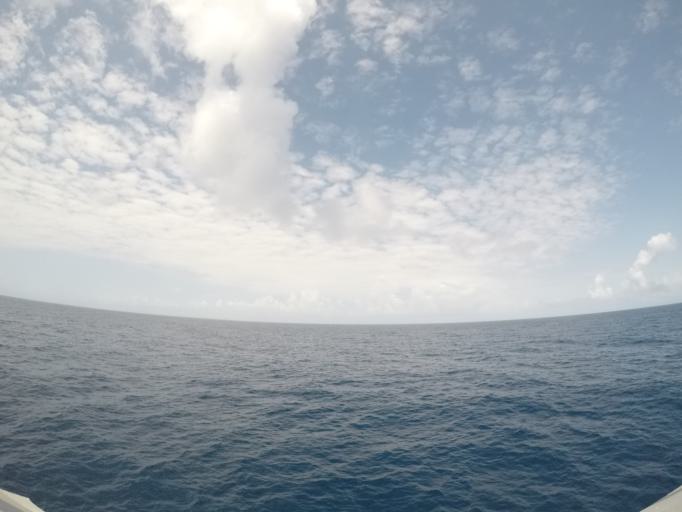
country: TZ
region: Zanzibar North
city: Nungwi
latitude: -5.5735
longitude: 39.3656
